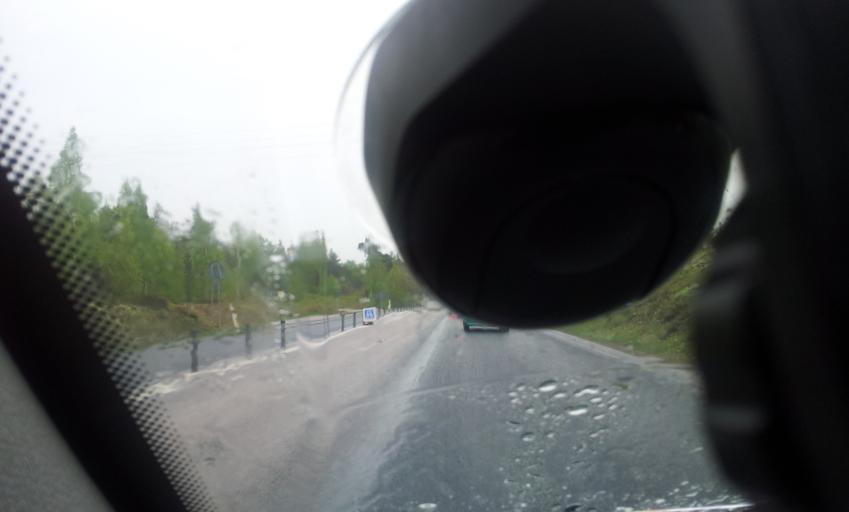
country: SE
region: Kalmar
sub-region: Oskarshamns Kommun
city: Oskarshamn
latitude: 57.3644
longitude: 16.4938
